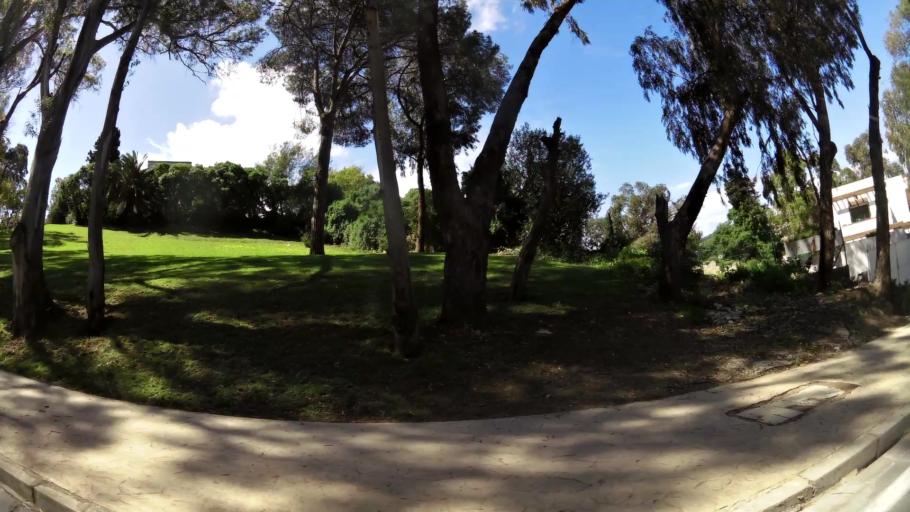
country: MA
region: Tanger-Tetouan
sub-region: Tanger-Assilah
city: Tangier
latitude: 35.7798
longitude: -5.8339
